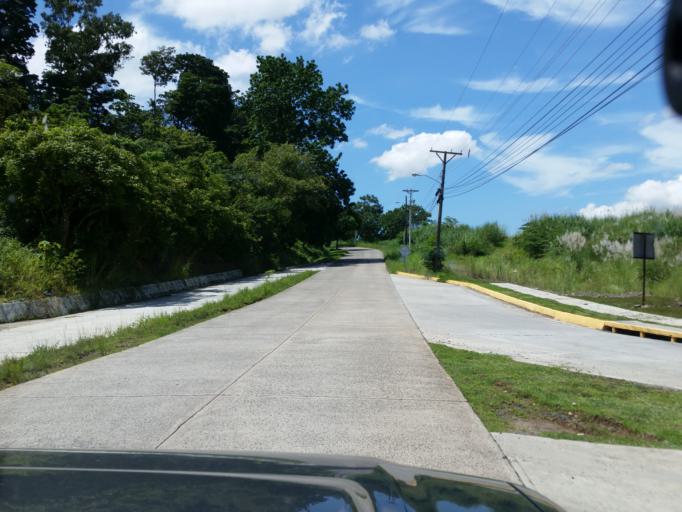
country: PA
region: Panama
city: San Miguelito
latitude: 9.0742
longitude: -79.4704
